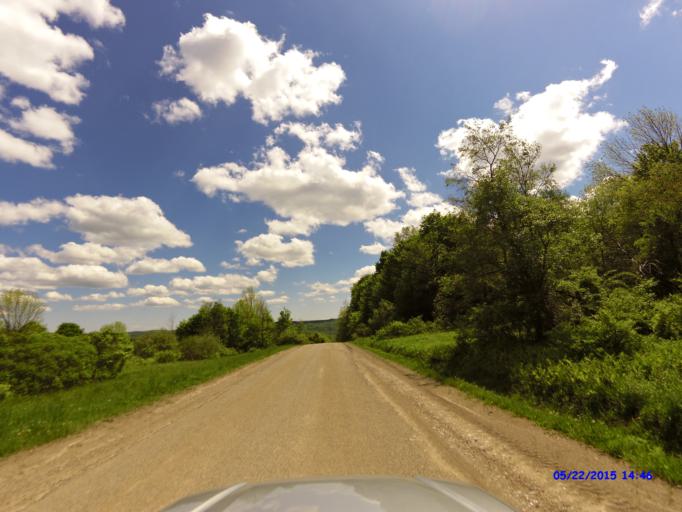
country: US
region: New York
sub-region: Cattaraugus County
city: Franklinville
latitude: 42.3562
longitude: -78.5845
